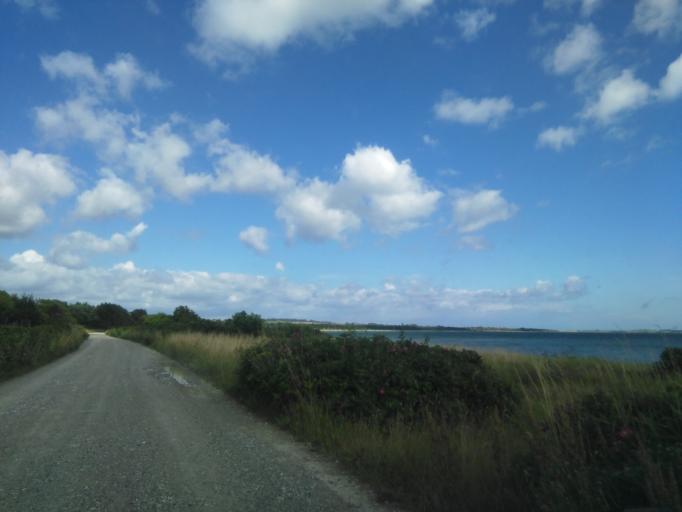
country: DK
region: Central Jutland
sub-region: Syddjurs Kommune
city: Ronde
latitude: 56.1806
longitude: 10.4429
